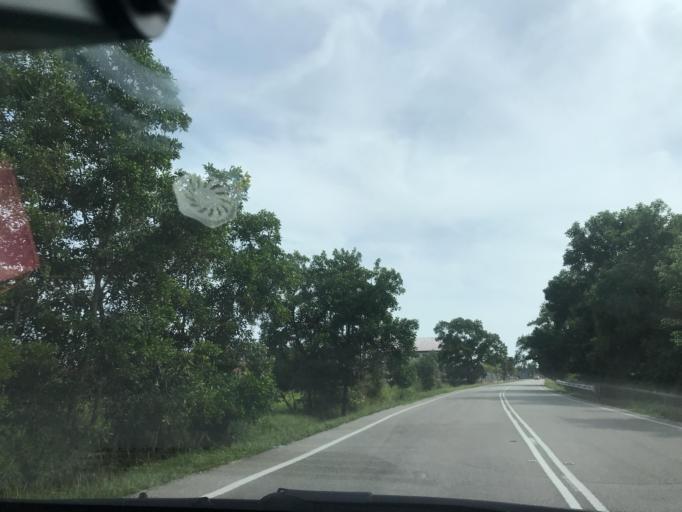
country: MY
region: Kelantan
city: Tumpat
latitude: 6.1987
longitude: 102.1556
